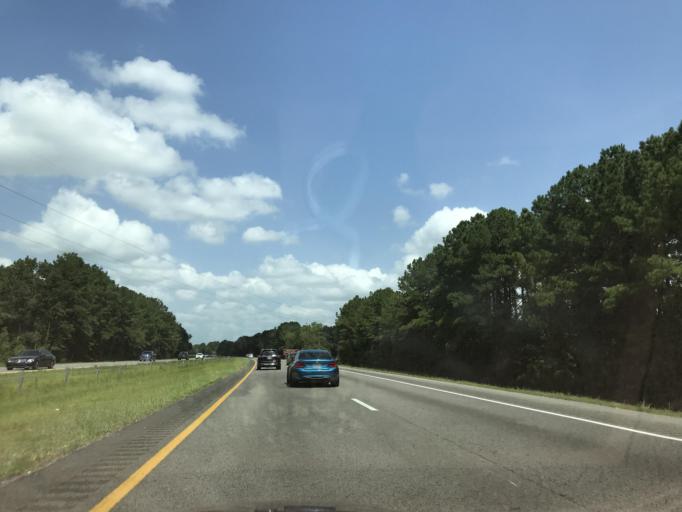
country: US
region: North Carolina
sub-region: Pender County
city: Rocky Point
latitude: 34.4164
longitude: -77.8693
